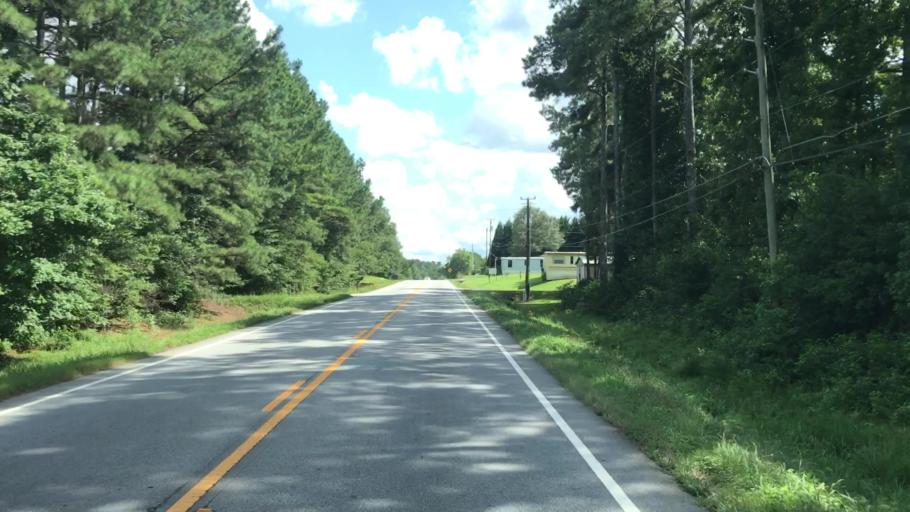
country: US
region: Georgia
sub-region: Newton County
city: Oxford
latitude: 33.6792
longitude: -83.8505
